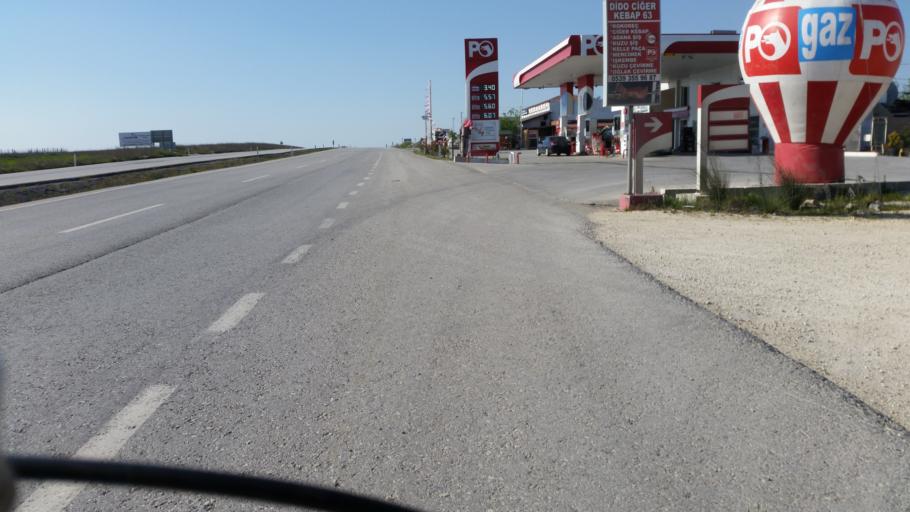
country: TR
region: Tekirdag
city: Cerkezkoey
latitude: 41.3406
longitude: 27.9654
